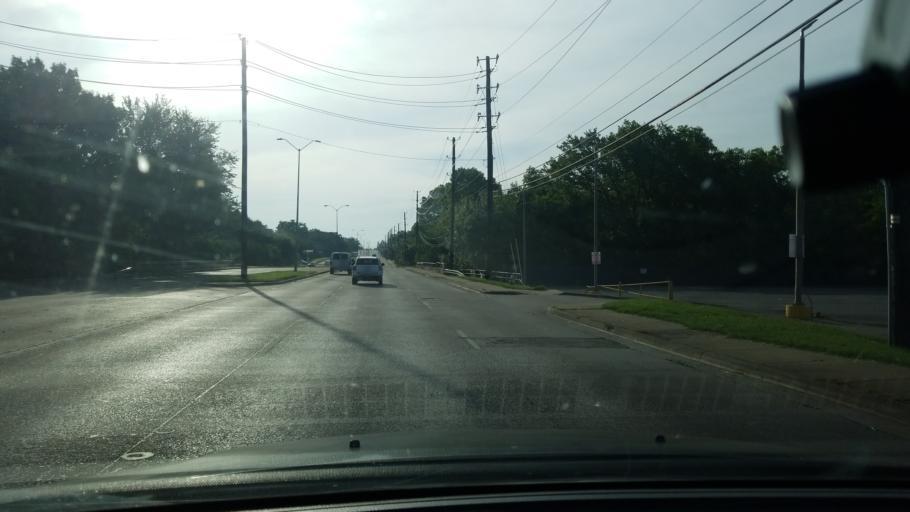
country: US
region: Texas
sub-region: Dallas County
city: Balch Springs
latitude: 32.7341
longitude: -96.6644
